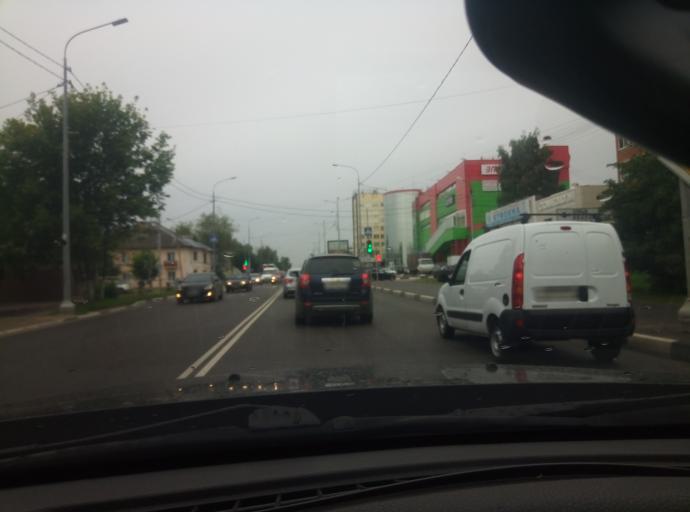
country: RU
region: Moskovskaya
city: Serpukhov
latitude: 54.9149
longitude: 37.4383
